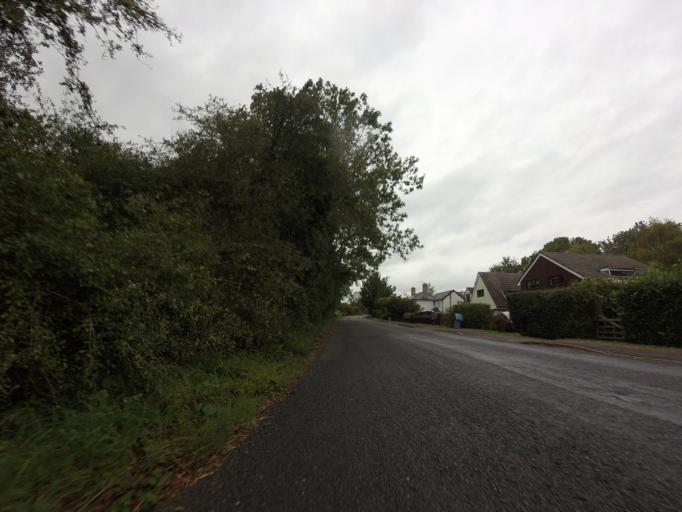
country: GB
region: England
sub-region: Cambridgeshire
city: Comberton
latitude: 52.1560
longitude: 0.0070
